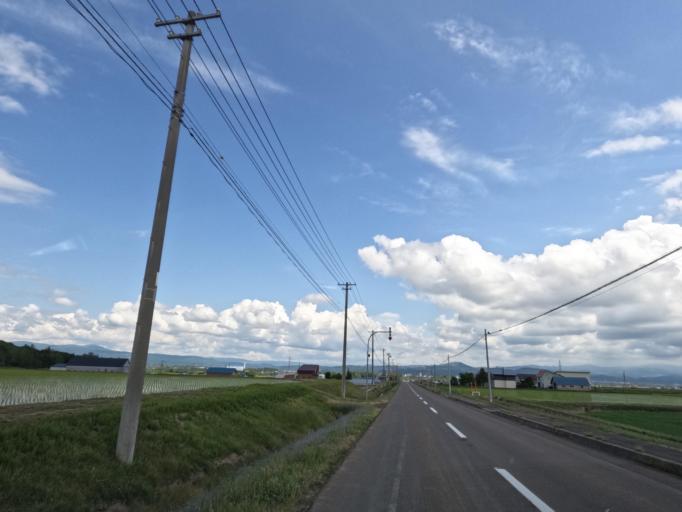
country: JP
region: Hokkaido
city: Takikawa
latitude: 43.5755
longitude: 141.8505
